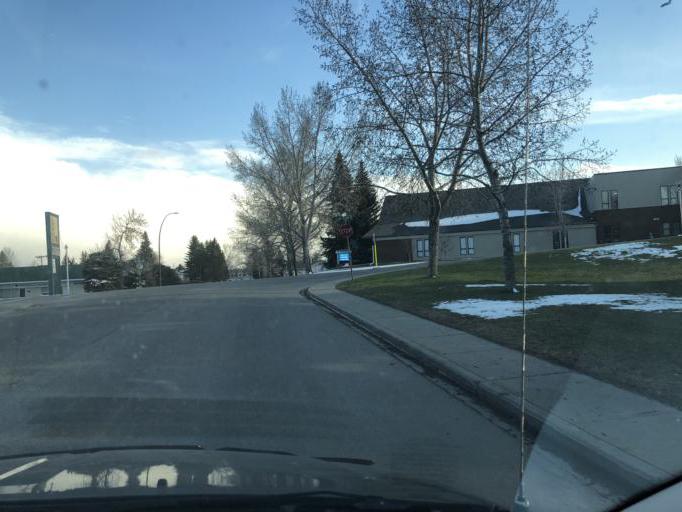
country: CA
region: Alberta
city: Calgary
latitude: 50.9429
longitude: -114.0338
